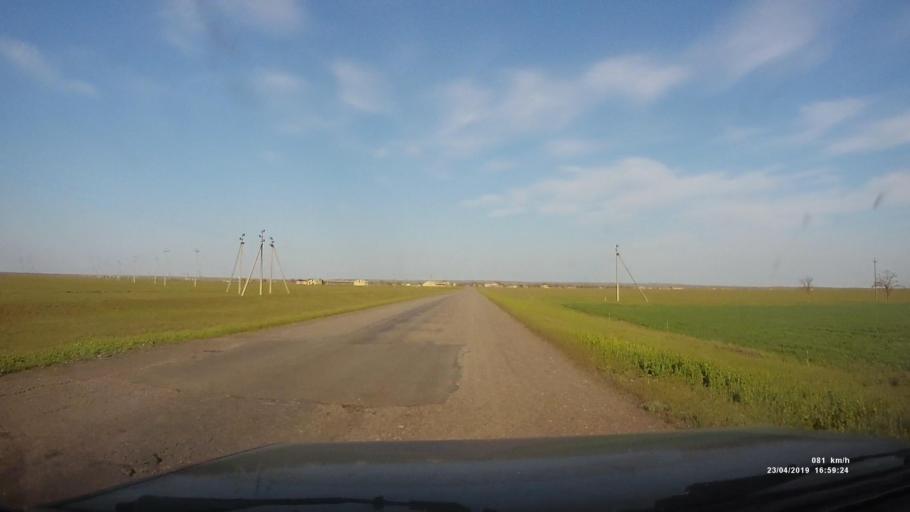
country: RU
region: Kalmykiya
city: Priyutnoye
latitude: 46.3082
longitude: 43.3895
